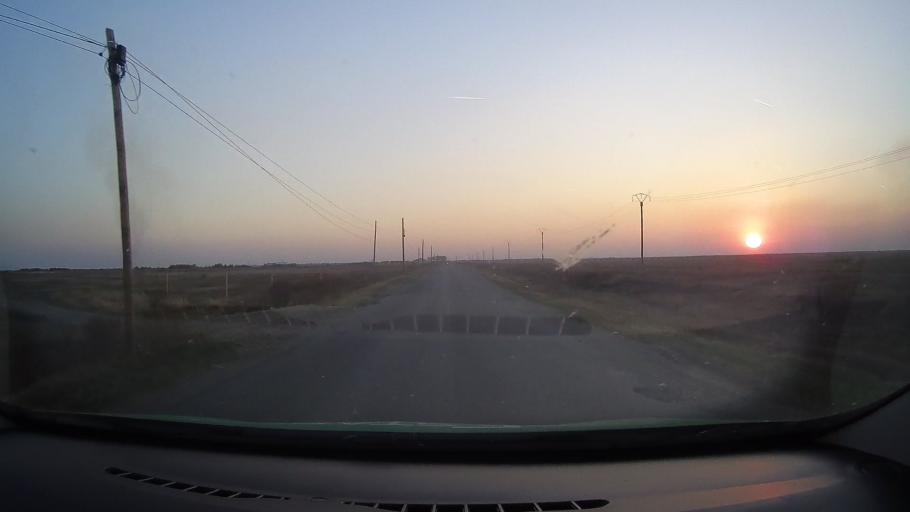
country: RO
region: Arad
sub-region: Comuna Olari
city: Olari
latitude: 46.3767
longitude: 21.5379
